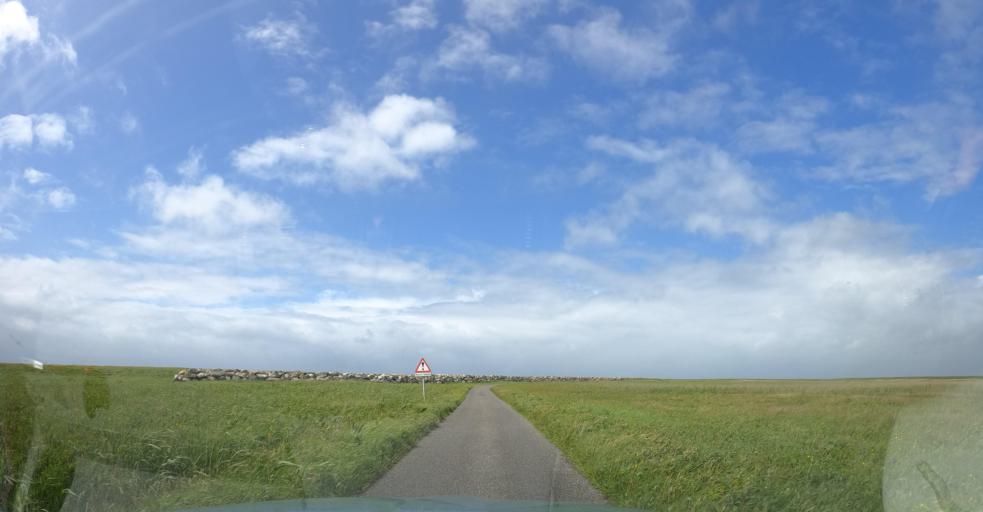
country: GB
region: Scotland
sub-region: Eilean Siar
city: Isle of South Uist
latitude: 57.2806
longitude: -7.4183
